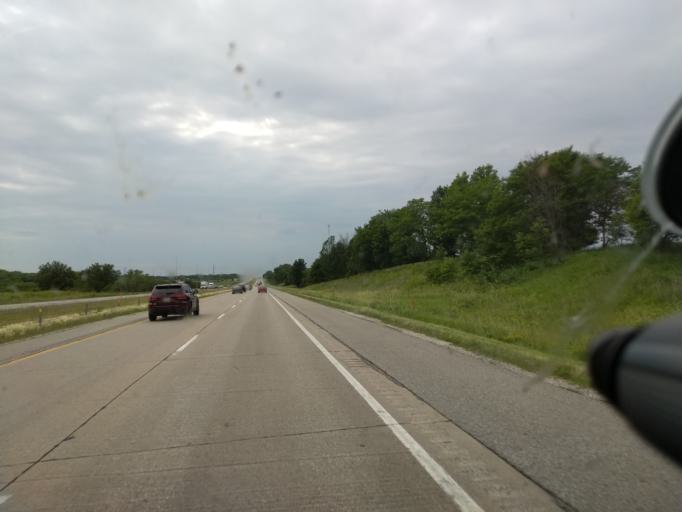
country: US
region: Iowa
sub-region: Dallas County
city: Waukee
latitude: 41.5586
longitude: -93.9027
